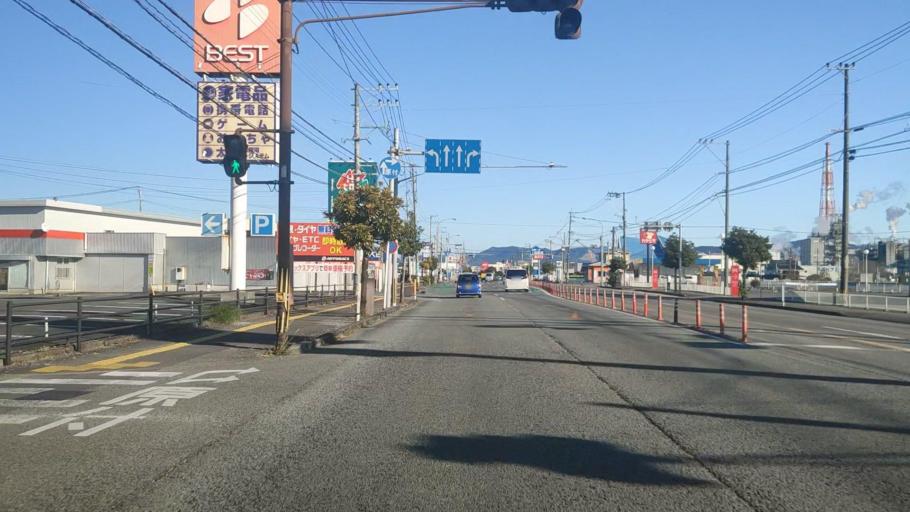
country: JP
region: Miyazaki
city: Nobeoka
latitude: 32.5614
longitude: 131.6810
